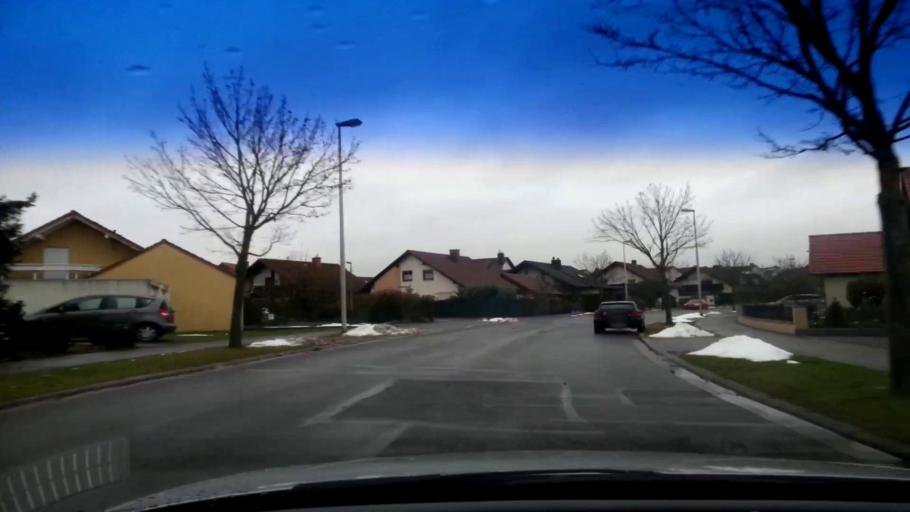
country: DE
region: Bavaria
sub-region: Upper Franconia
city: Gundelsheim
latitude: 49.9396
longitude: 10.9123
